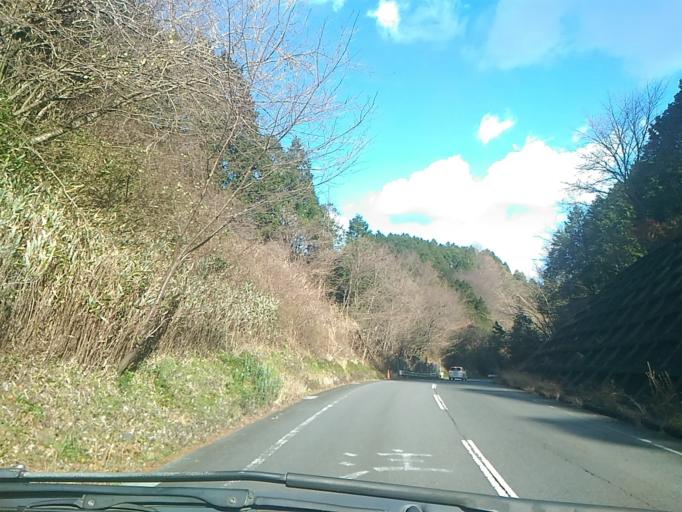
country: JP
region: Fukushima
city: Iwaki
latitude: 37.0083
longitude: 140.8208
